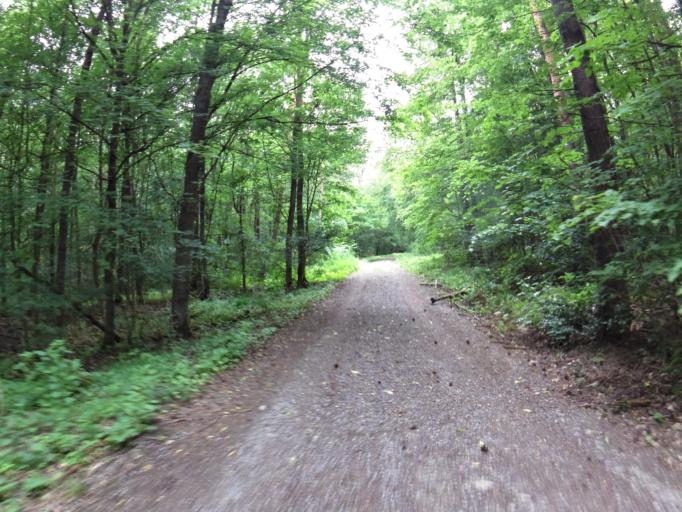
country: DE
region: Bavaria
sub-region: Regierungsbezirk Unterfranken
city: Hettstadt
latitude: 49.8224
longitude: 9.8290
